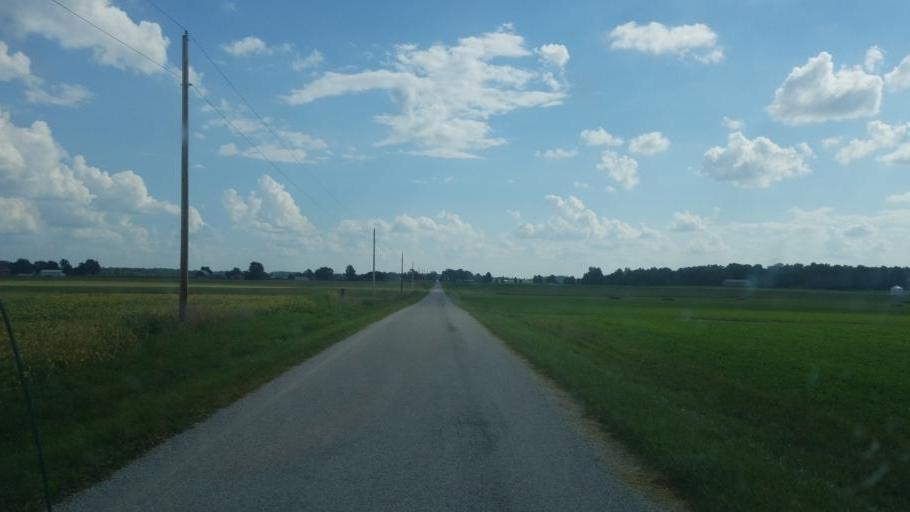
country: US
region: Ohio
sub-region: Huron County
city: Willard
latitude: 40.9896
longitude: -82.8160
